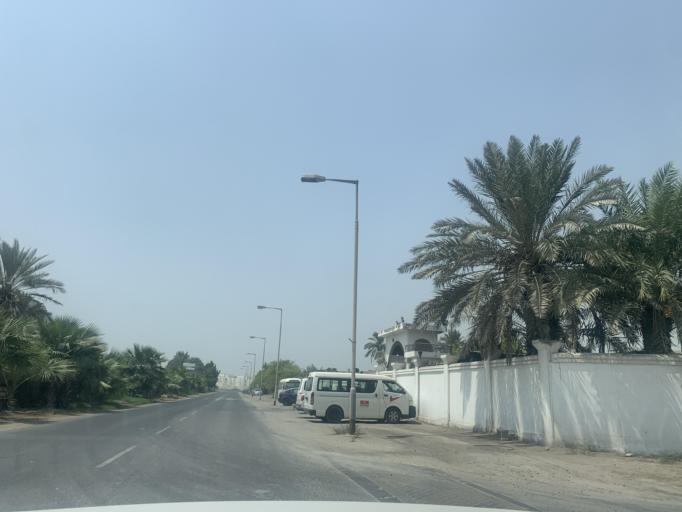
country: BH
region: Central Governorate
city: Madinat Hamad
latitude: 26.1257
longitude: 50.4714
